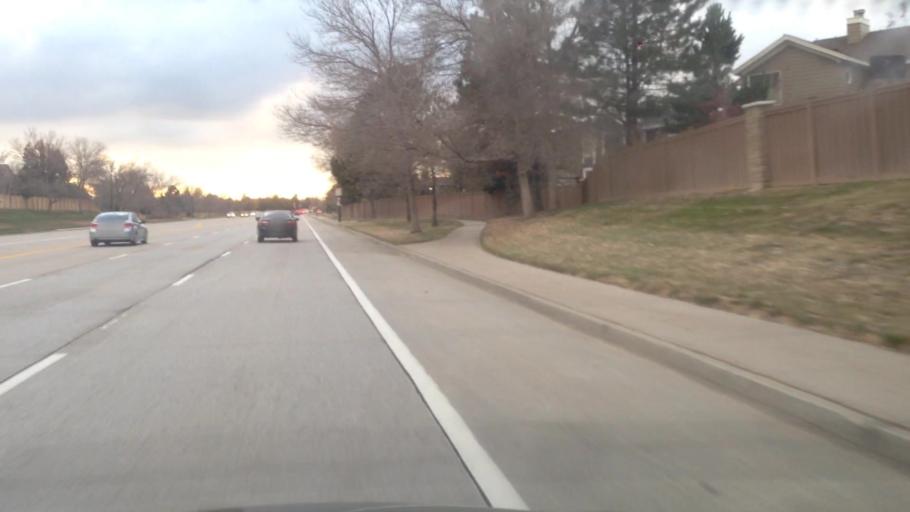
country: US
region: Colorado
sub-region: Douglas County
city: Carriage Club
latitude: 39.5440
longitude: -104.9243
